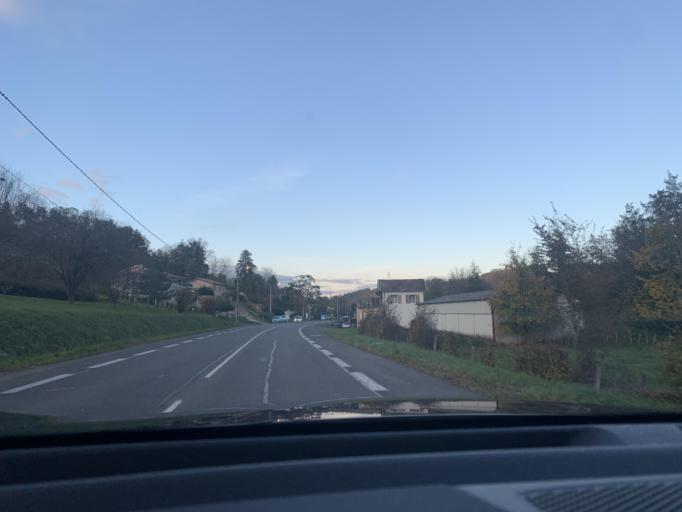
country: FR
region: Rhone-Alpes
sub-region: Departement du Rhone
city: Liergues
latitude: 45.9523
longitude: 4.6636
